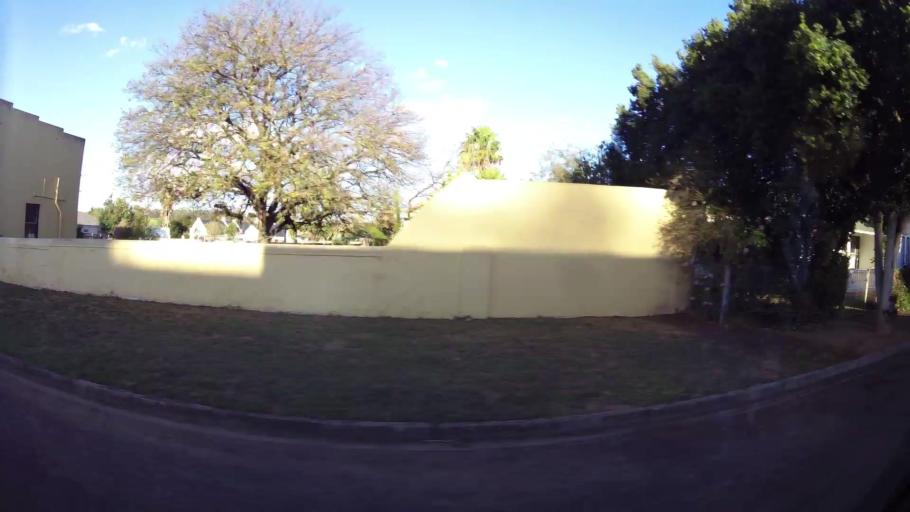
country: ZA
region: Western Cape
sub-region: Eden District Municipality
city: Riversdale
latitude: -34.0871
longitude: 20.9612
